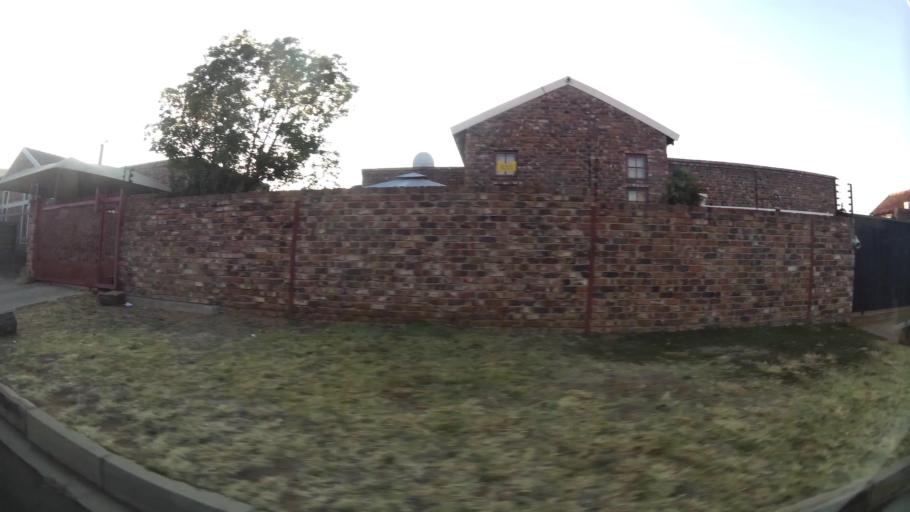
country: ZA
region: Orange Free State
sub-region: Mangaung Metropolitan Municipality
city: Bloemfontein
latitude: -29.1032
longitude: 26.1639
